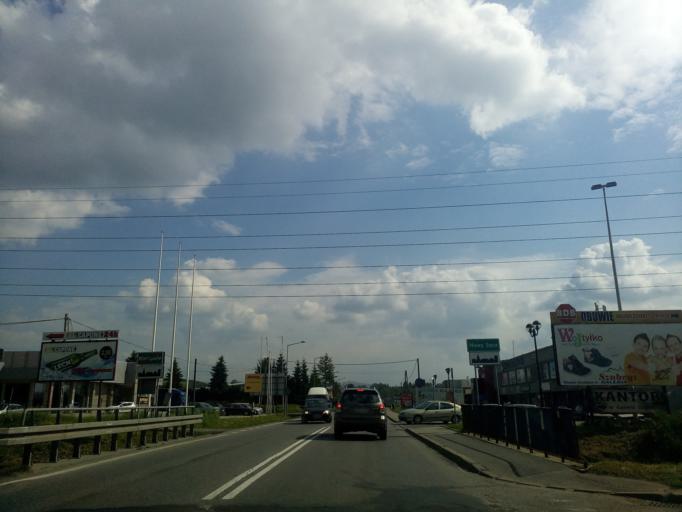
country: PL
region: Lesser Poland Voivodeship
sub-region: Powiat nowosadecki
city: Nowy Sacz
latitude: 49.6575
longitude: 20.6896
